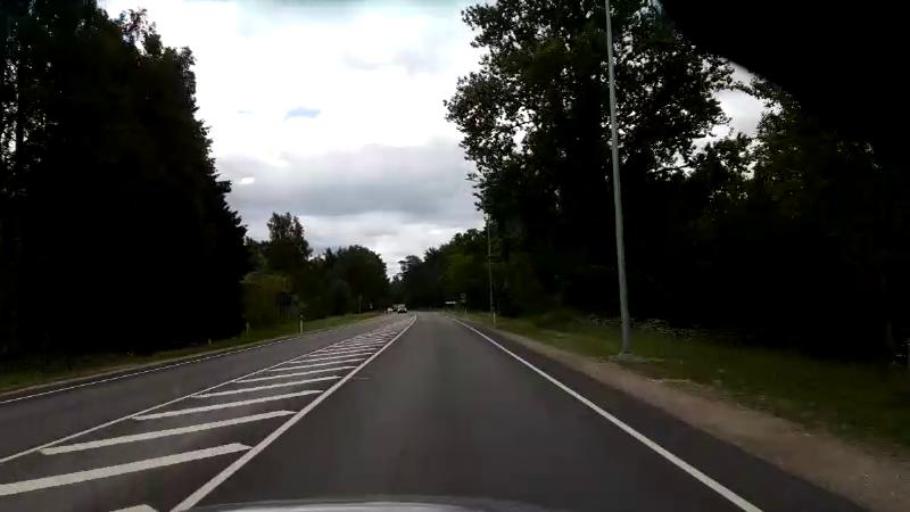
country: EE
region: Paernumaa
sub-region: Paikuse vald
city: Paikuse
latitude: 58.3189
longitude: 24.5995
